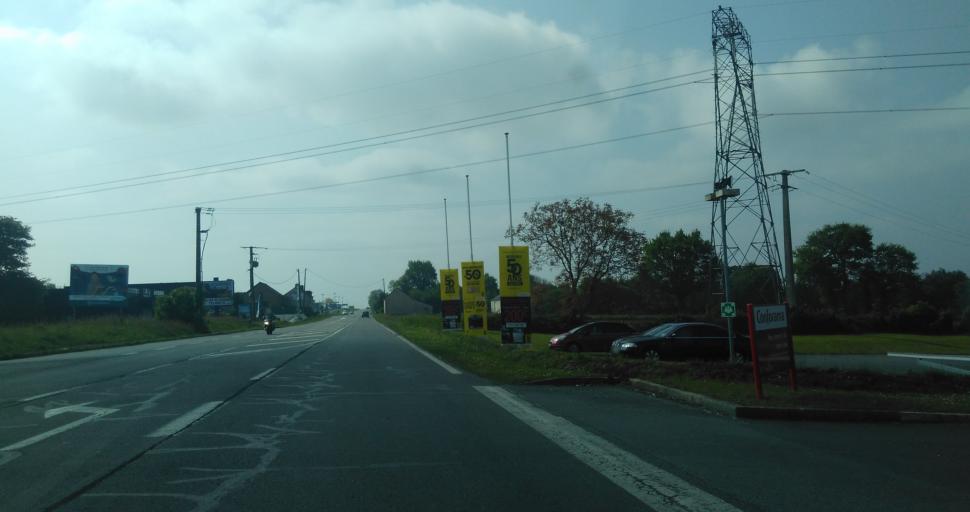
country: FR
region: Brittany
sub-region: Departement d'Ille-et-Vilaine
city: La Chapelle-des-Fougeretz
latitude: 48.1894
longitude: -1.7277
